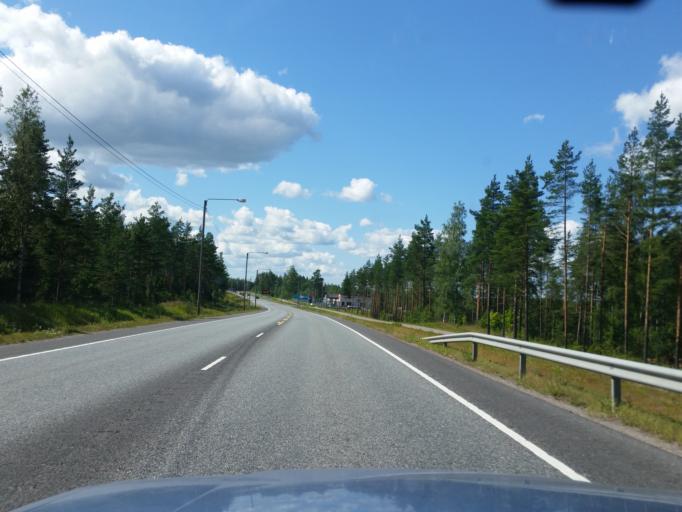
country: FI
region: Uusimaa
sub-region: Helsinki
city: Vihti
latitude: 60.3217
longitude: 24.2662
